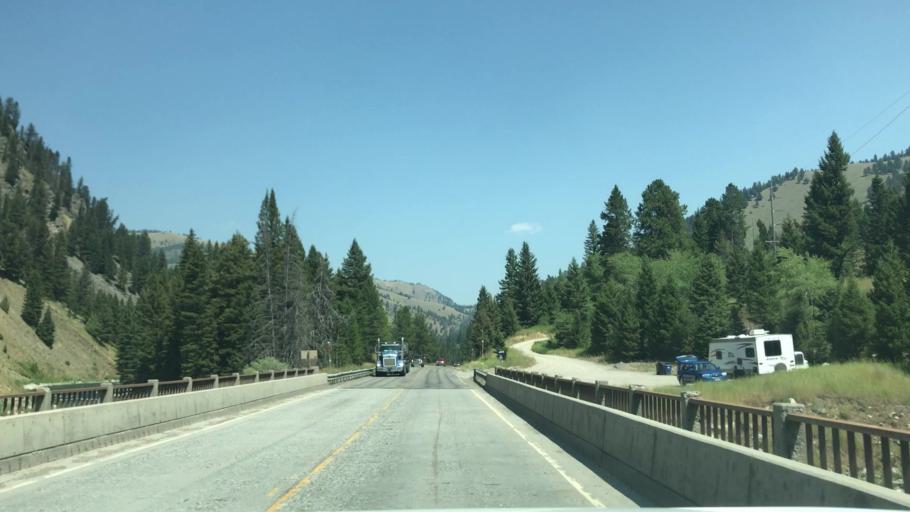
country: US
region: Montana
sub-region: Gallatin County
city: Big Sky
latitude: 45.2816
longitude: -111.2258
